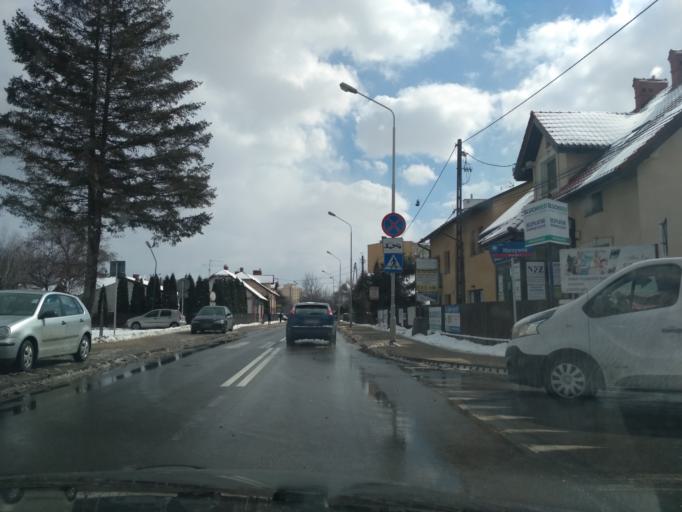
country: PL
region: Subcarpathian Voivodeship
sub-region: Rzeszow
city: Rzeszow
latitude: 50.0334
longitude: 22.0150
